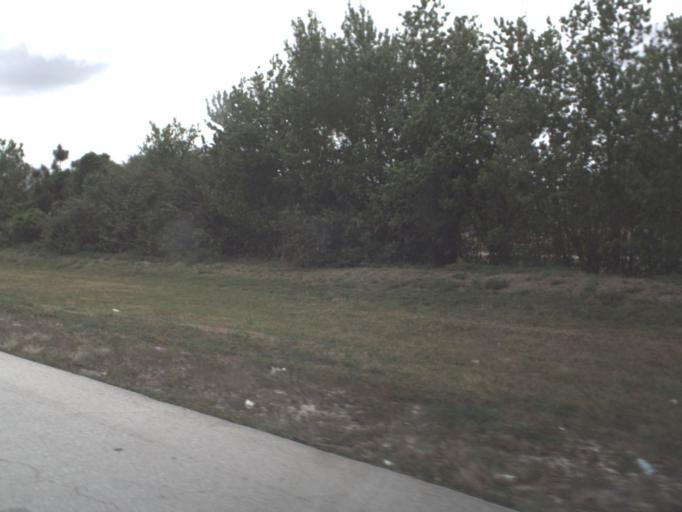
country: US
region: Florida
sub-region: Brevard County
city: June Park
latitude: 28.1601
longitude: -80.7061
